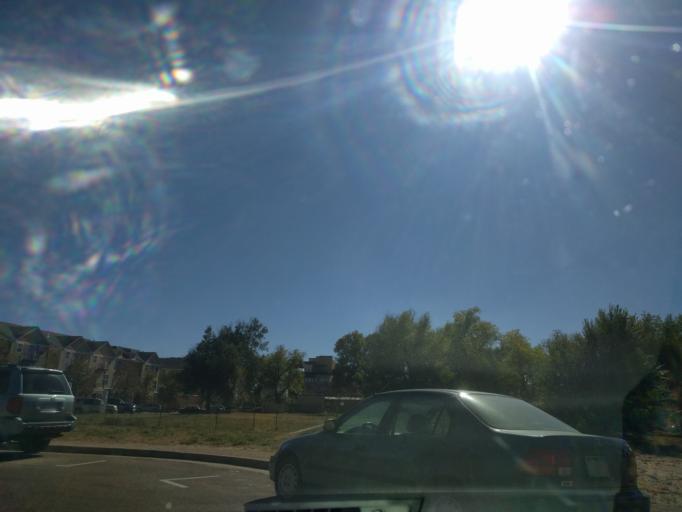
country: US
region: Colorado
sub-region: El Paso County
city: Colorado Springs
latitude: 38.8230
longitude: -104.8210
